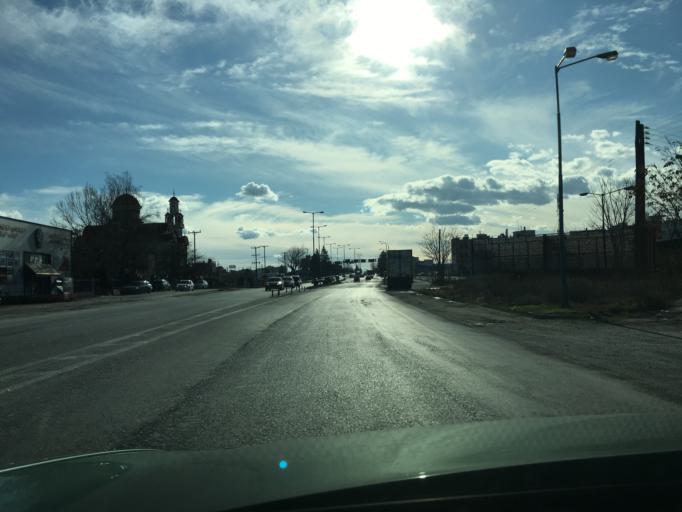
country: GR
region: Thessaly
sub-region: Nomos Larisis
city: Larisa
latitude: 39.6355
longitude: 22.4358
